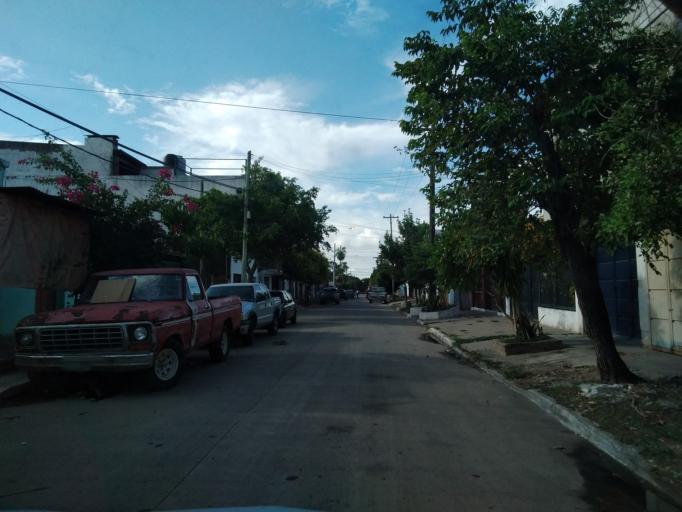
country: AR
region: Corrientes
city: Corrientes
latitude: -27.4646
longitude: -58.8140
